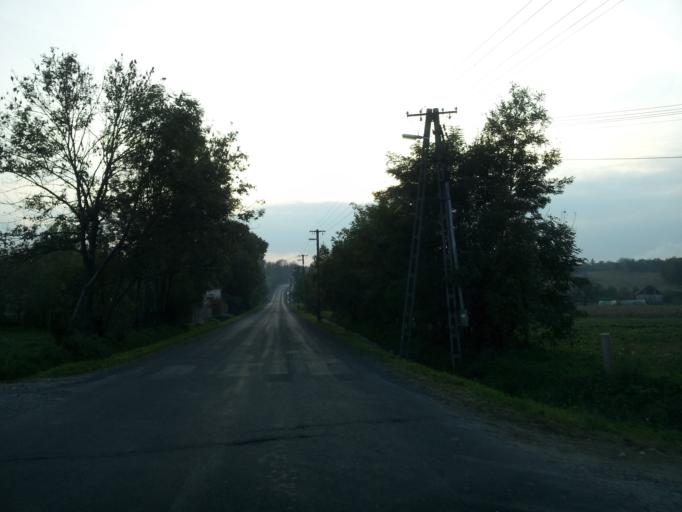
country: HU
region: Komarom-Esztergom
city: Kisber
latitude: 47.4687
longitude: 17.9093
